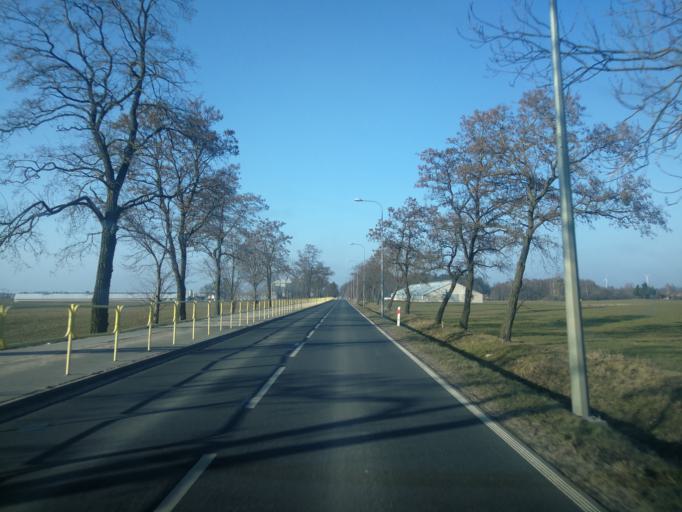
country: PL
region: Warmian-Masurian Voivodeship
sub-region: Powiat ilawski
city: Lubawa
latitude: 53.4879
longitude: 19.7600
